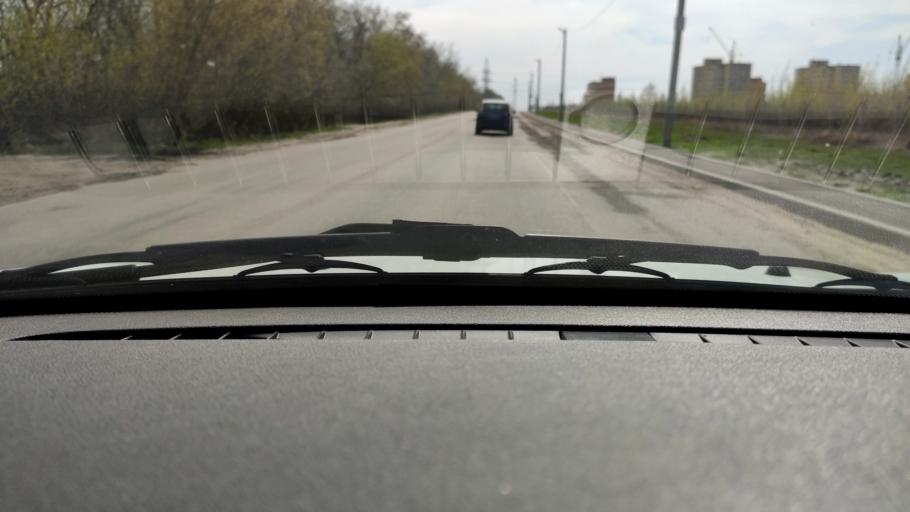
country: RU
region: Voronezj
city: Novaya Usman'
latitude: 51.6328
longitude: 39.3330
